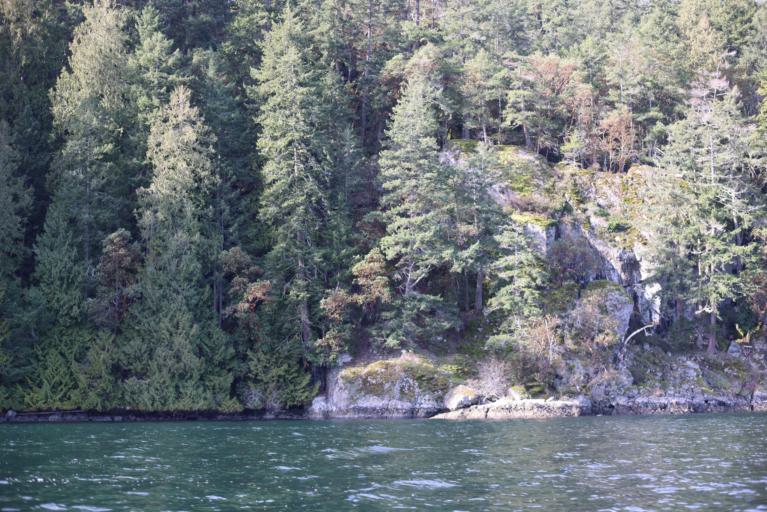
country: CA
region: British Columbia
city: North Cowichan
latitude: 48.7901
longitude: -123.5637
